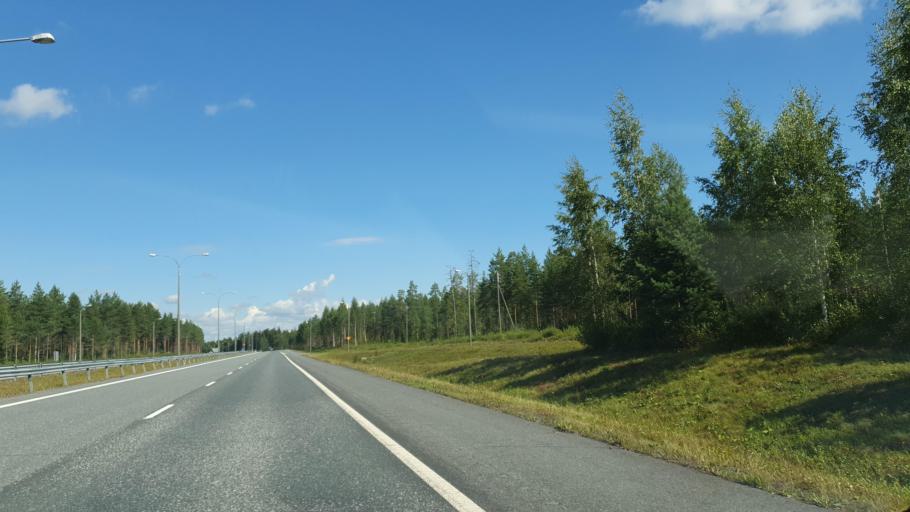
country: FI
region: Northern Savo
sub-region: Ylae-Savo
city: Iisalmi
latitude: 63.5486
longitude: 27.2526
